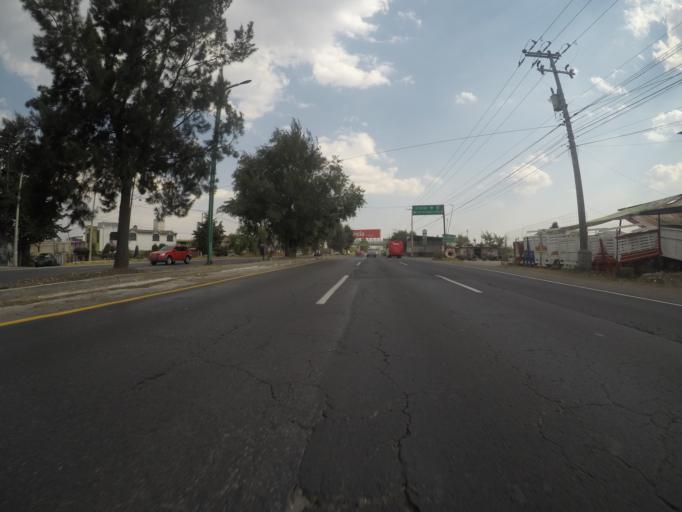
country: MX
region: Morelos
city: San Miguel Totocuitlapilco
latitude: 19.2294
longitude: -99.5957
